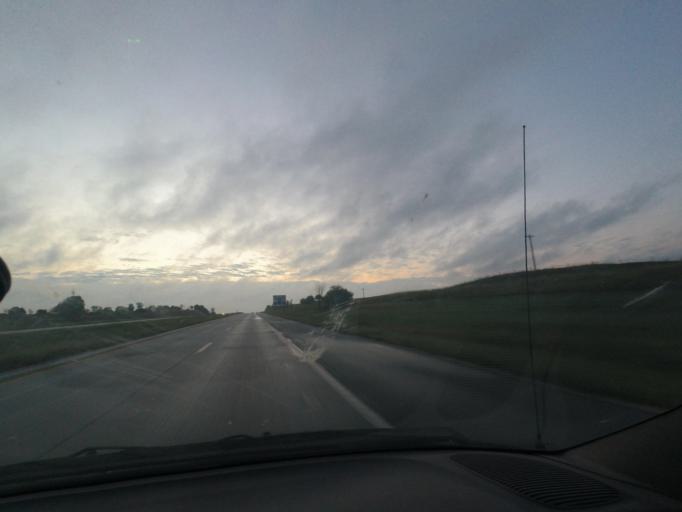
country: US
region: Missouri
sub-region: Linn County
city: Marceline
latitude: 39.7611
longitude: -92.9569
